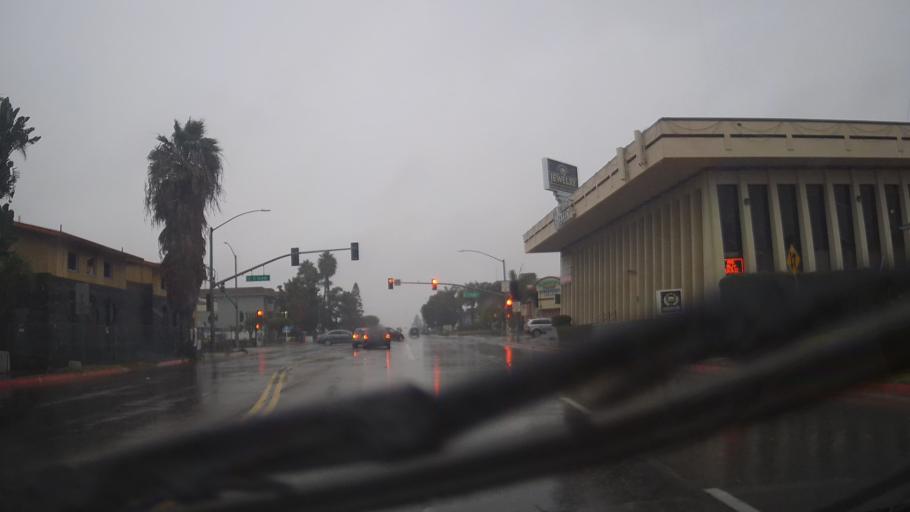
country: US
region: California
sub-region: San Diego County
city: Chula Vista
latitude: 32.6426
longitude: -117.0848
